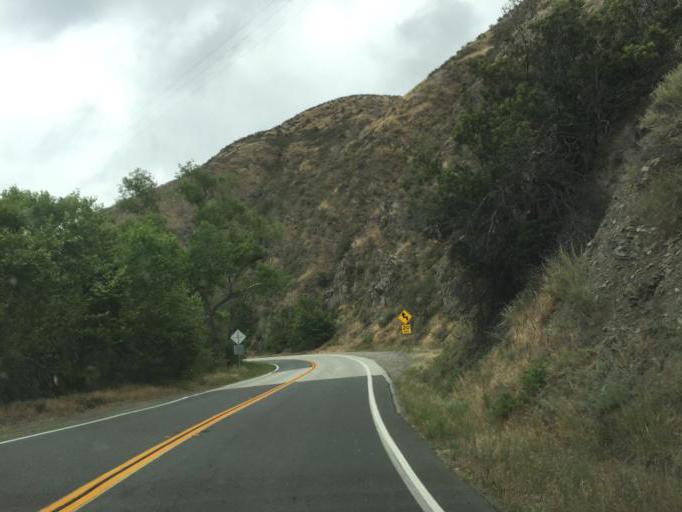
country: US
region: California
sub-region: Los Angeles County
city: Green Valley
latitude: 34.5141
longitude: -118.4495
